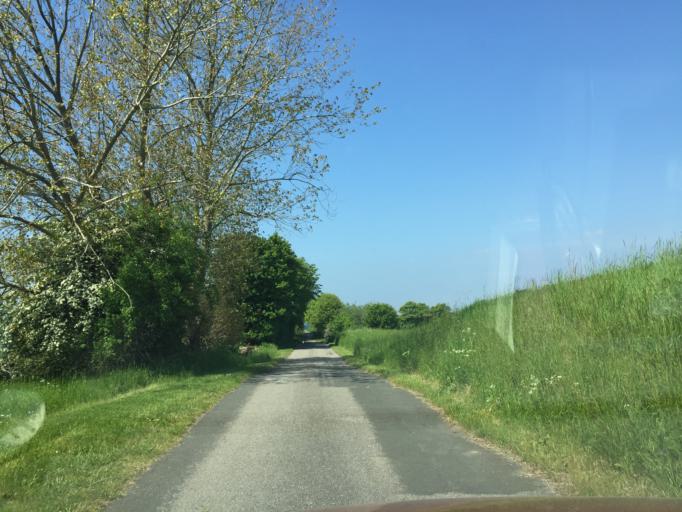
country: DK
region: South Denmark
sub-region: Langeland Kommune
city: Rudkobing
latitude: 55.0152
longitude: 10.8316
